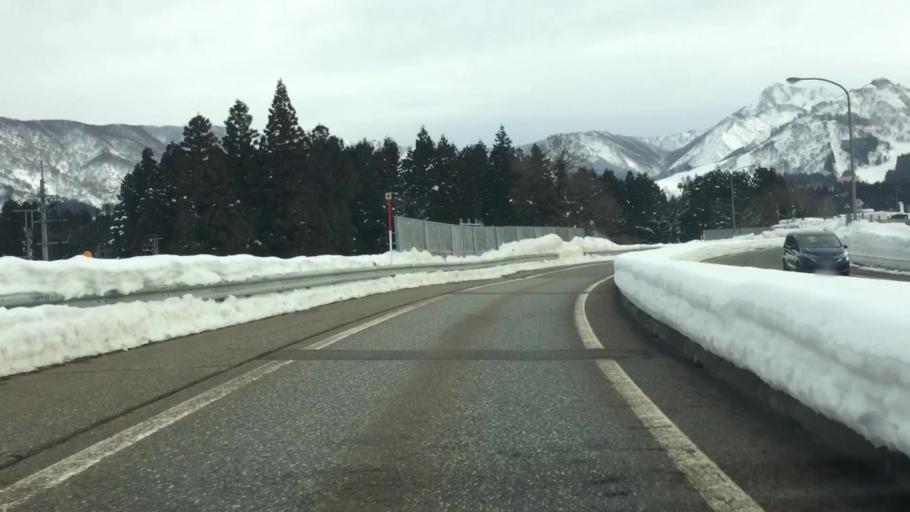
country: JP
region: Niigata
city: Shiozawa
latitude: 36.9957
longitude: 138.8214
